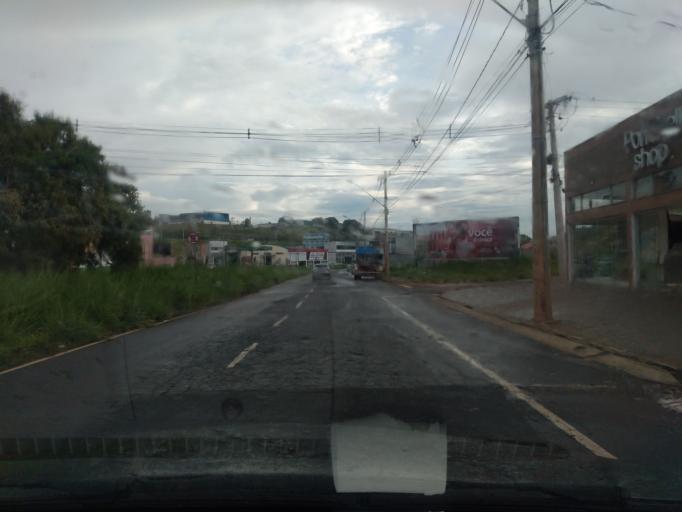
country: BR
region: Minas Gerais
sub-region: Varginha
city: Varginha
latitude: -21.5721
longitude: -45.4468
